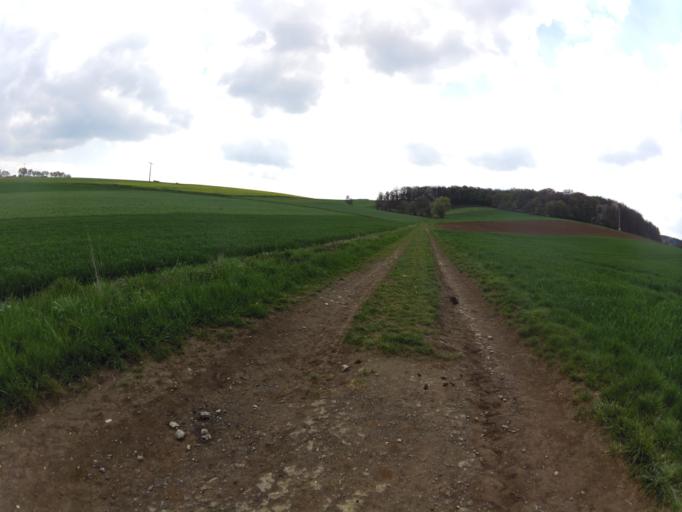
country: DE
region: Bavaria
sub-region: Regierungsbezirk Unterfranken
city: Hettstadt
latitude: 49.7986
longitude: 9.7921
